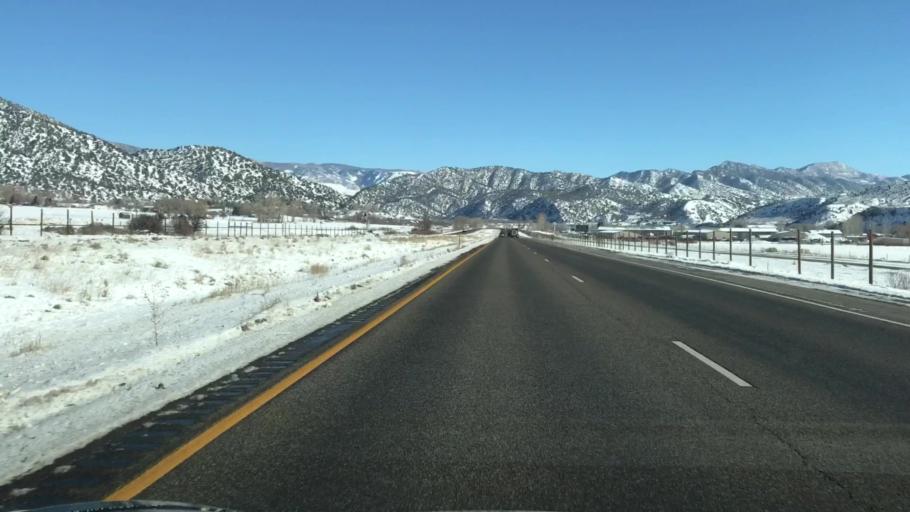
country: US
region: Colorado
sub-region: Garfield County
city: New Castle
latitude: 39.5540
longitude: -107.5791
